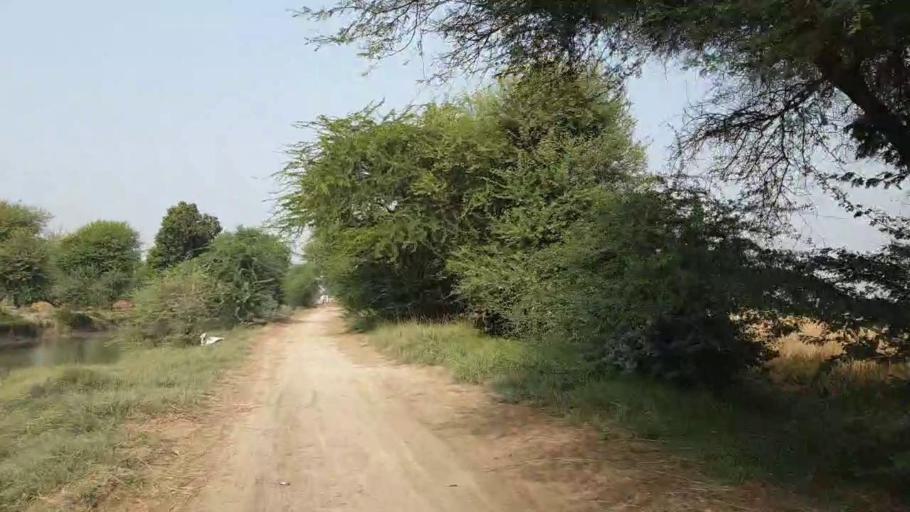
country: PK
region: Sindh
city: Kario
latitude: 24.8305
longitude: 68.5463
